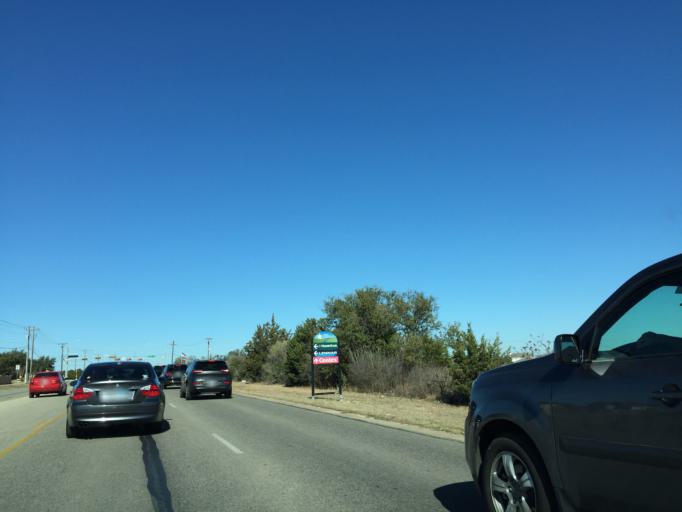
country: US
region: Texas
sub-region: Williamson County
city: Leander
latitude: 30.5674
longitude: -97.8668
